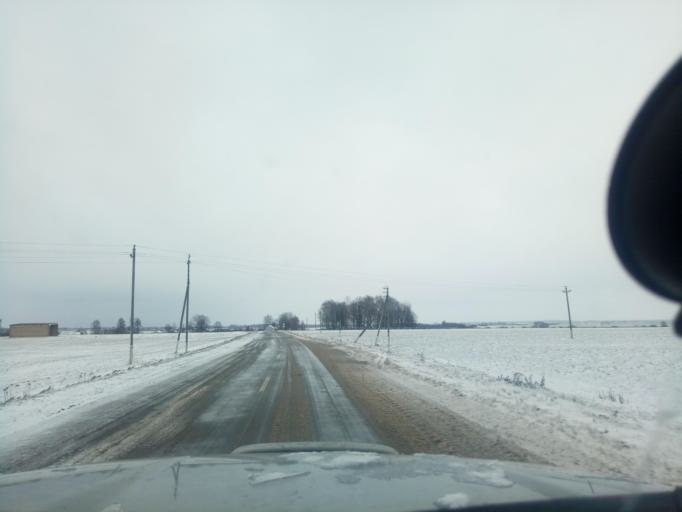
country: BY
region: Minsk
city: Klyetsk
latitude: 53.0388
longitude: 26.7446
